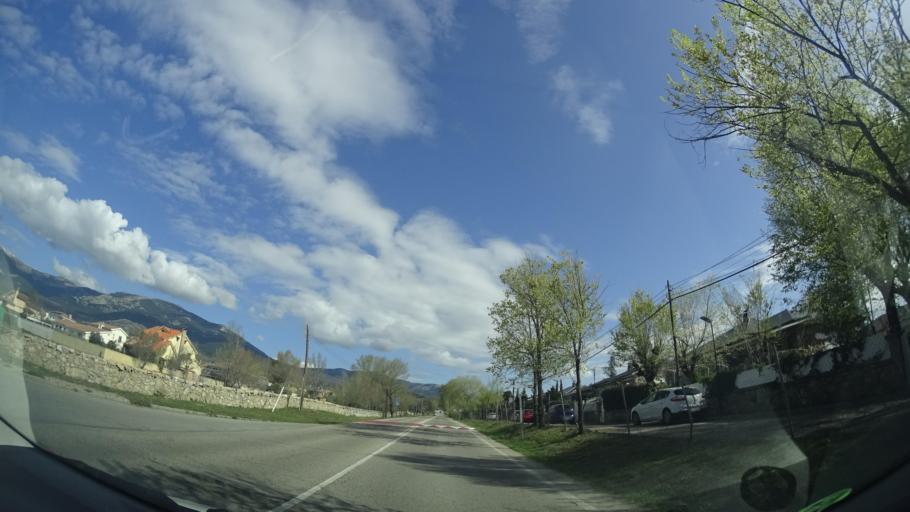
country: ES
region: Madrid
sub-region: Provincia de Madrid
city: Miraflores de la Sierra
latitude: 40.7597
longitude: -3.7825
